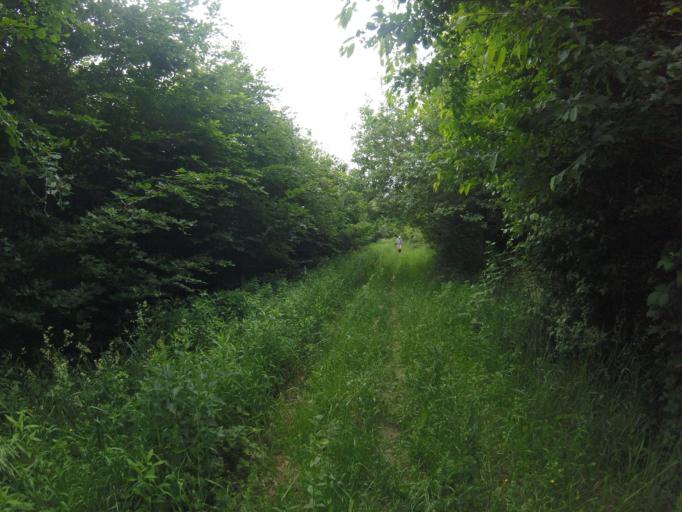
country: HU
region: Veszprem
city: Urkut
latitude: 47.0929
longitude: 17.6476
